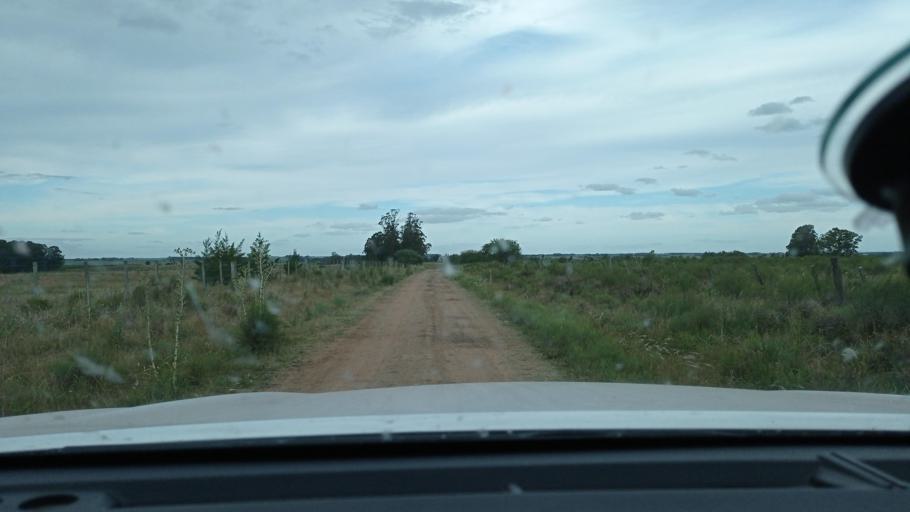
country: UY
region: Florida
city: Casupa
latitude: -34.1237
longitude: -55.8146
